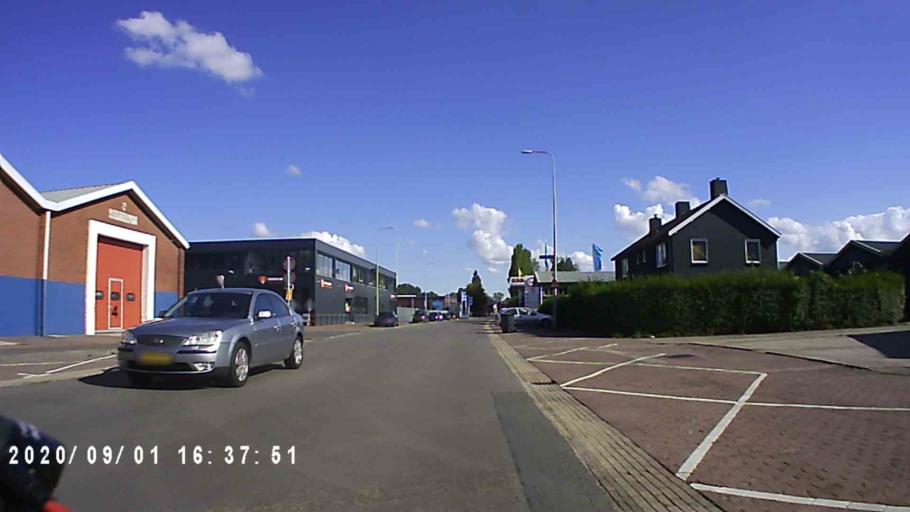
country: NL
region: Groningen
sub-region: Gemeente Groningen
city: Oosterpark
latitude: 53.2359
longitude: 6.5830
